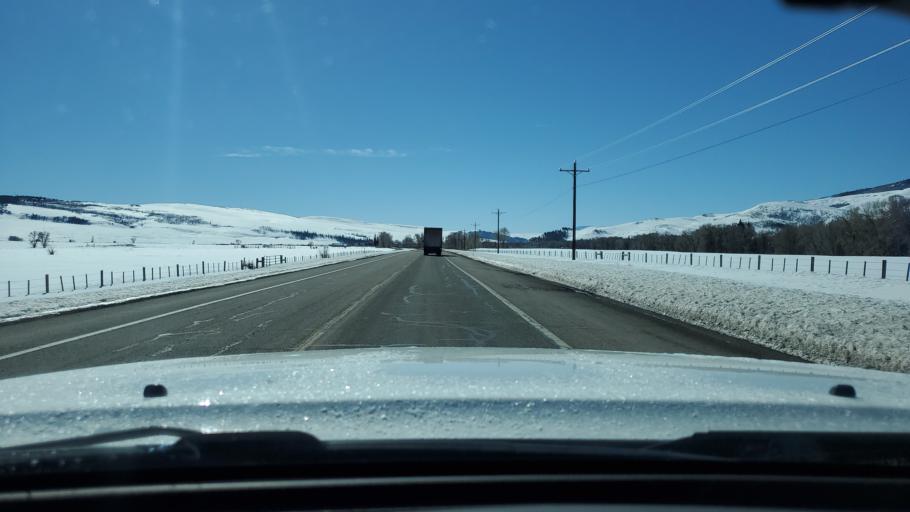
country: US
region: Colorado
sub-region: Gunnison County
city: Crested Butte
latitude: 38.7555
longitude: -106.8614
